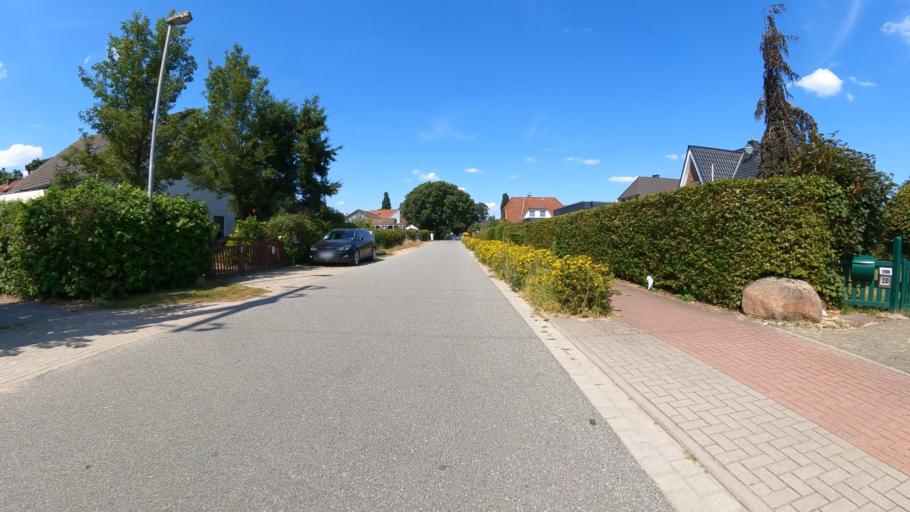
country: DE
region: Schleswig-Holstein
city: Ellerhoop
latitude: 53.7260
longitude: 9.7734
